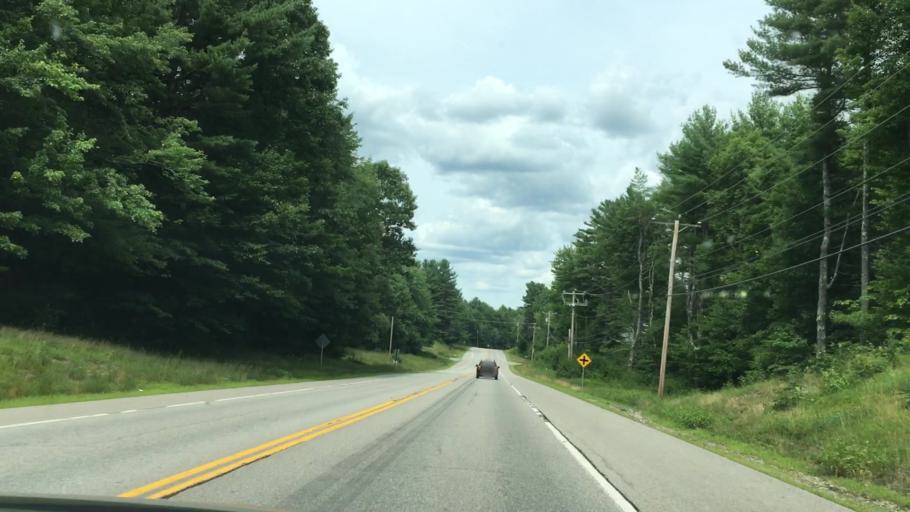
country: US
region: New Hampshire
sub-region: Cheshire County
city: Jaffrey
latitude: 42.8346
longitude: -71.9895
